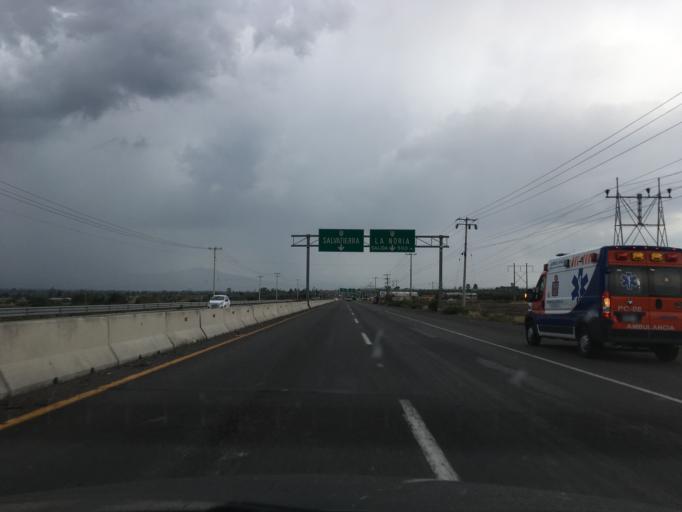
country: MX
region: Guanajuato
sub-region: Tarimoro
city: San Juan Bautista Cacalote
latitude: 20.3558
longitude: -100.8021
